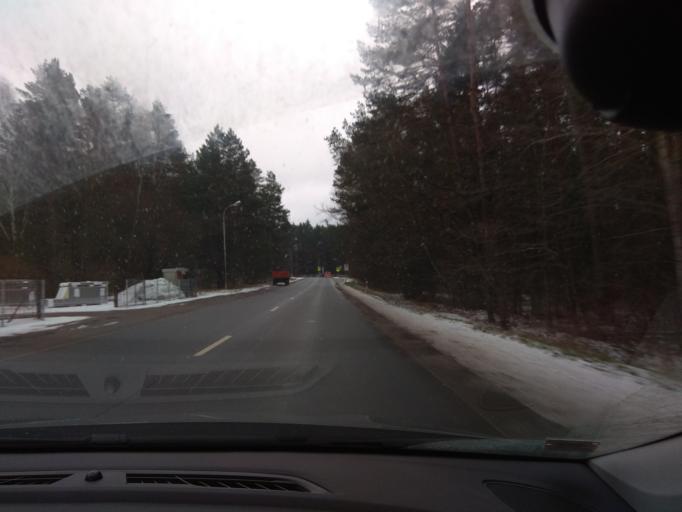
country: LT
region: Vilnius County
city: Lazdynai
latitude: 54.6408
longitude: 25.1768
